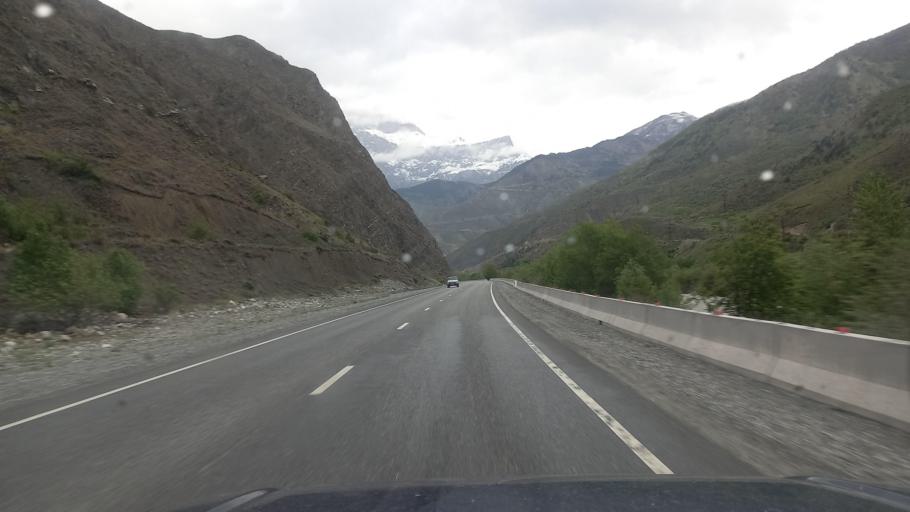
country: RU
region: North Ossetia
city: Mizur
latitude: 42.8574
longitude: 44.1149
